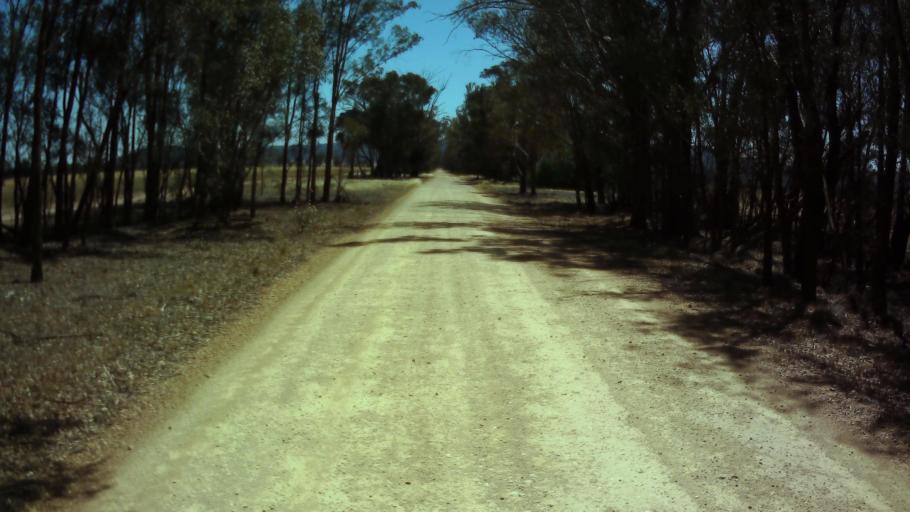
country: AU
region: New South Wales
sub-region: Weddin
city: Grenfell
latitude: -34.0188
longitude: 147.9622
